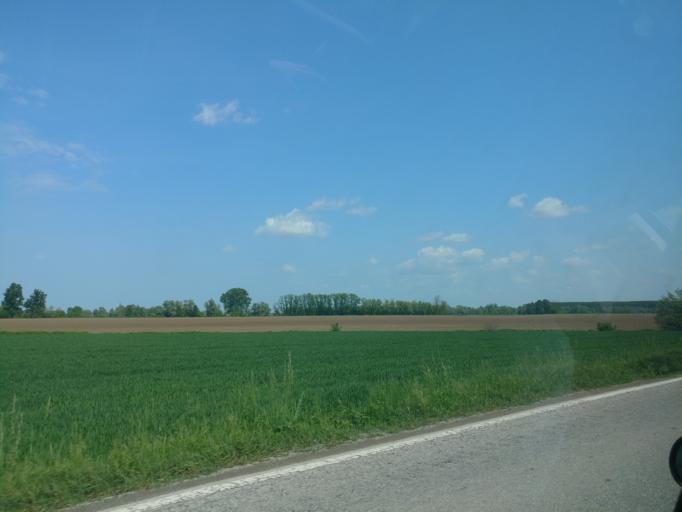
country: IT
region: Piedmont
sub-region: Provincia di Cuneo
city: Carde
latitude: 44.7207
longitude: 7.4405
